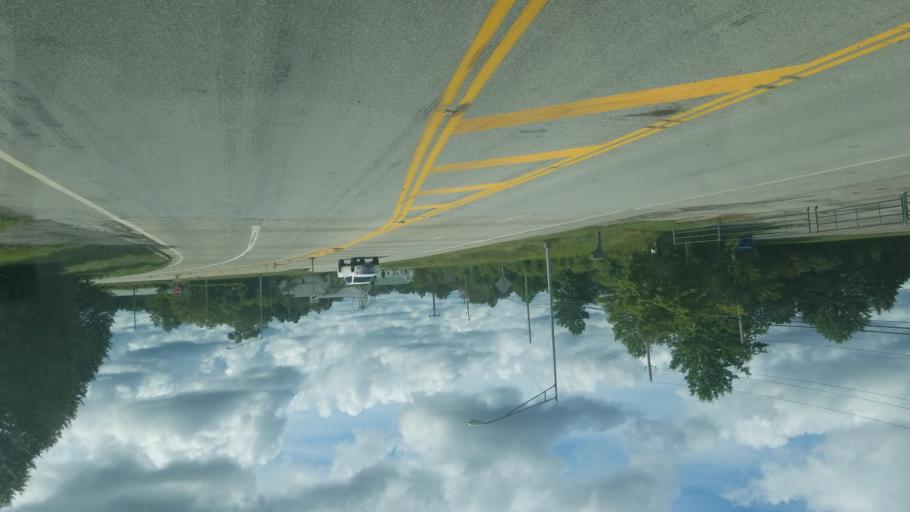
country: US
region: Ohio
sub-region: Lorain County
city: Oberlin
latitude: 41.2938
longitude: -82.1739
